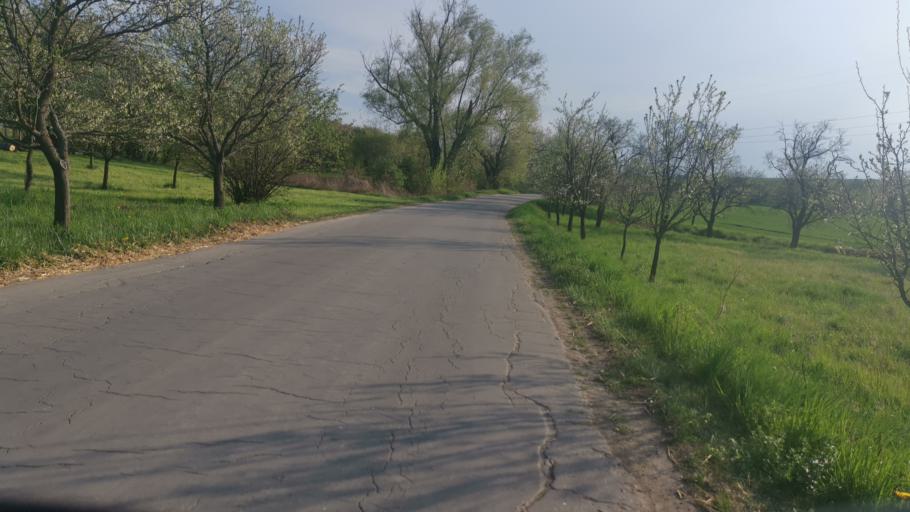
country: CZ
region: South Moravian
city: Petrov
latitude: 48.8588
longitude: 17.3093
